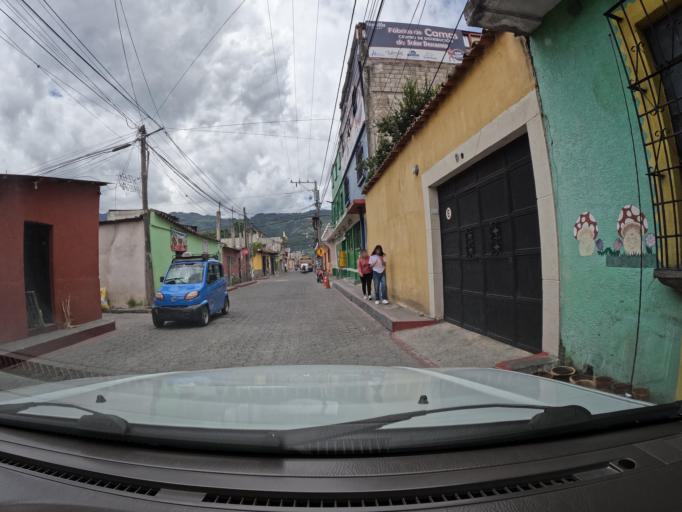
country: GT
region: Sacatepequez
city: Jocotenango
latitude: 14.5743
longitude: -90.7405
